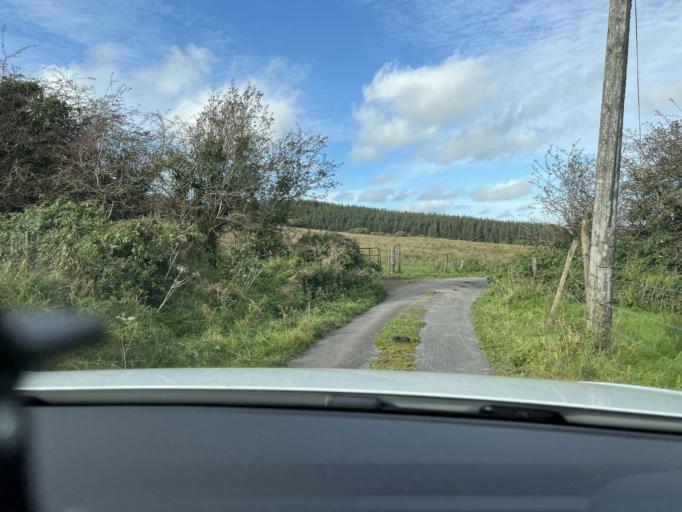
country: IE
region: Connaught
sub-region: Sligo
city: Ballymote
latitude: 54.0649
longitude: -8.4260
